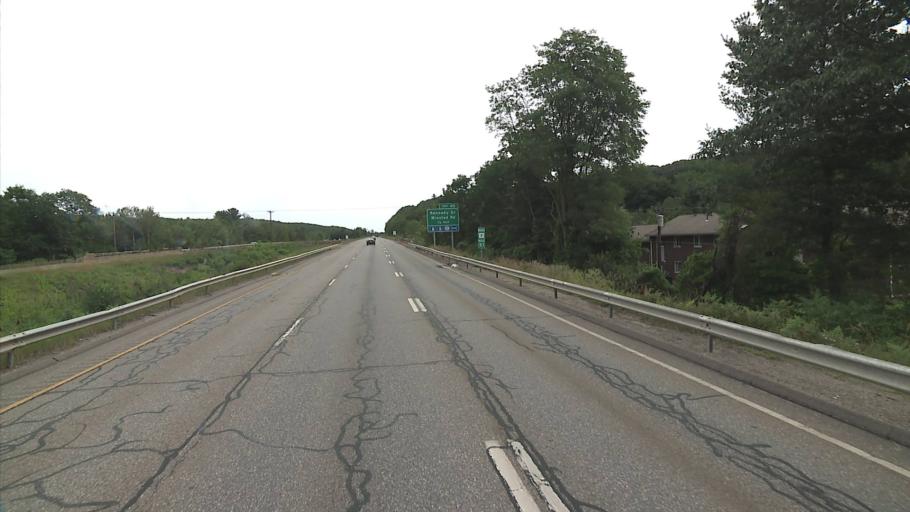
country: US
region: Connecticut
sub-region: Litchfield County
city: Torrington
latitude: 41.8204
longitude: -73.1115
